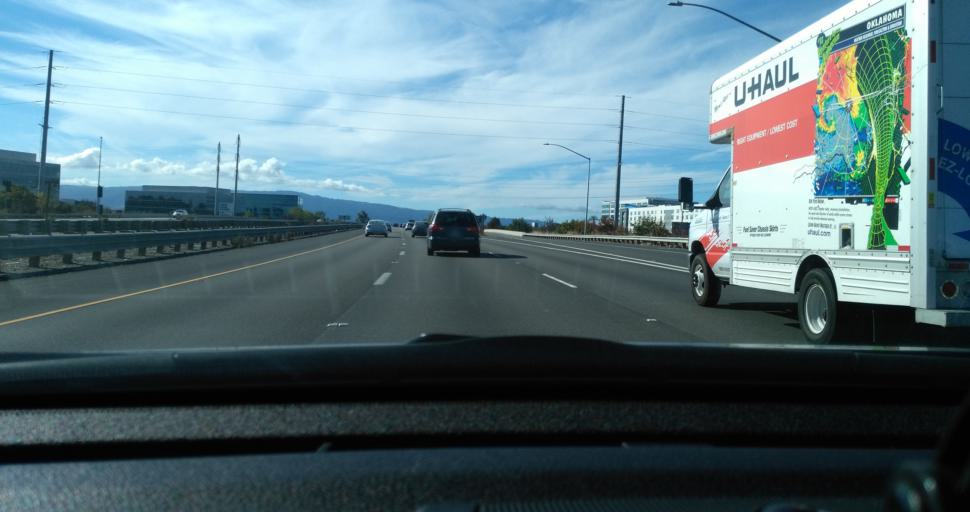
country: US
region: California
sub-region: Santa Clara County
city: Milpitas
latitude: 37.4185
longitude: -121.9715
